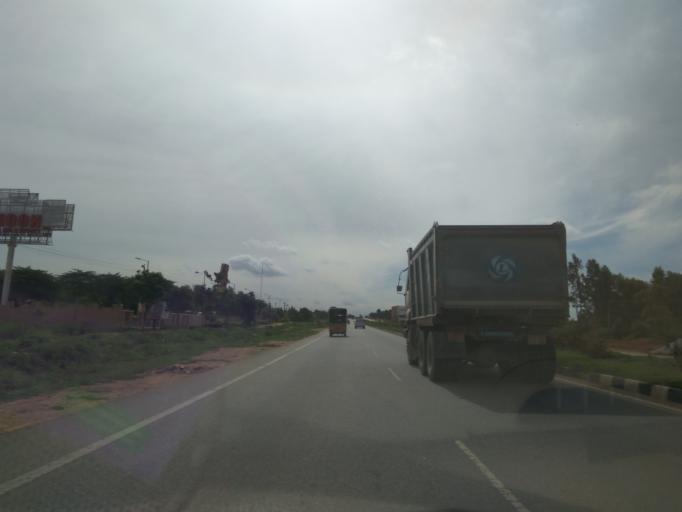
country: IN
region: Karnataka
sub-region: Bangalore Rural
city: Dasarahalli
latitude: 13.1329
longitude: 77.9509
